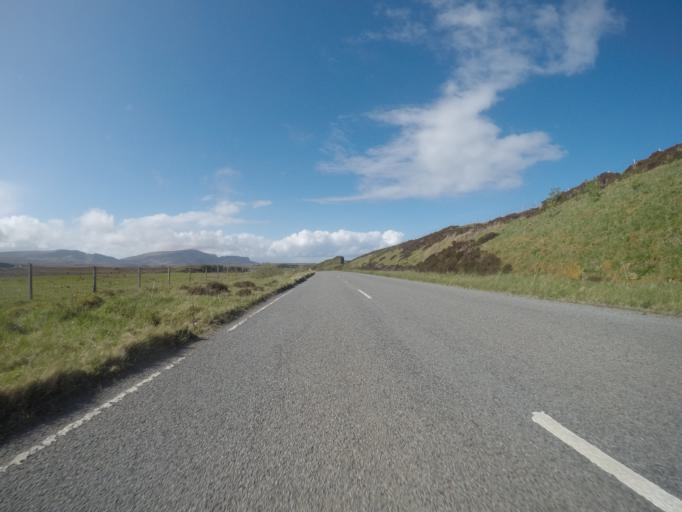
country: GB
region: Scotland
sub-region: Highland
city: Portree
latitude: 57.6003
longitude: -6.1644
